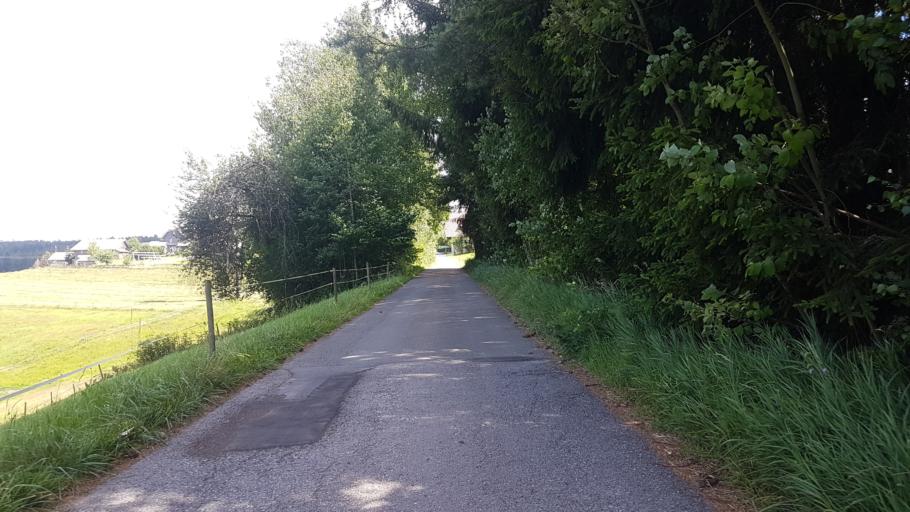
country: DE
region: Baden-Wuerttemberg
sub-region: Freiburg Region
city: Hardt
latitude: 48.1603
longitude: 8.4071
